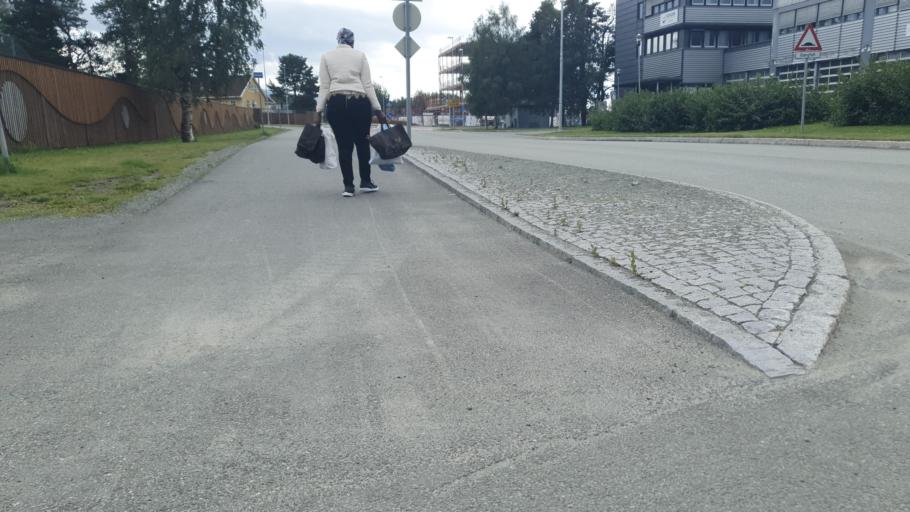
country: NO
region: Sor-Trondelag
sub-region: Trondheim
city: Trondheim
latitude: 63.3496
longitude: 10.3602
